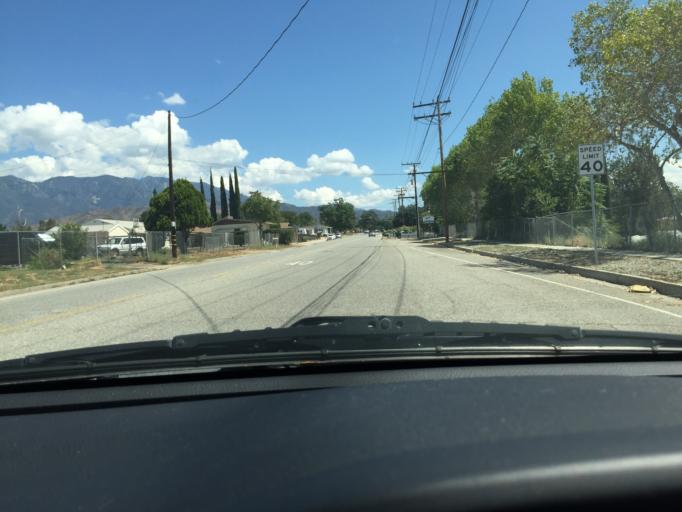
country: US
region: California
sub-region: Riverside County
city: Calimesa
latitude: 34.0157
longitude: -117.0595
